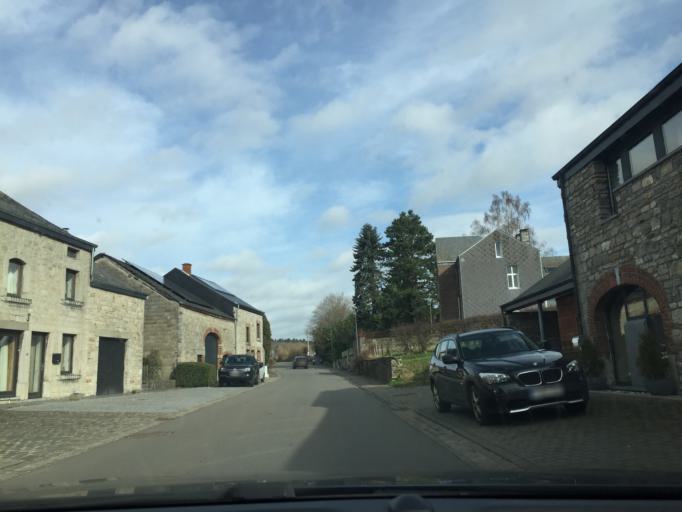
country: BE
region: Wallonia
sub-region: Province du Luxembourg
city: Hotton
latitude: 50.2859
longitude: 5.4812
